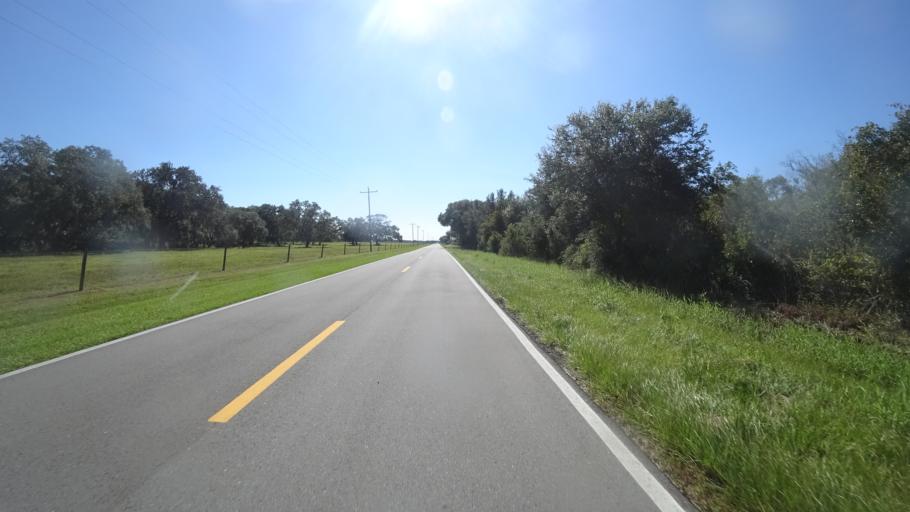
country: US
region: Florida
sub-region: Sarasota County
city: Lake Sarasota
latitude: 27.2854
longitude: -82.2156
